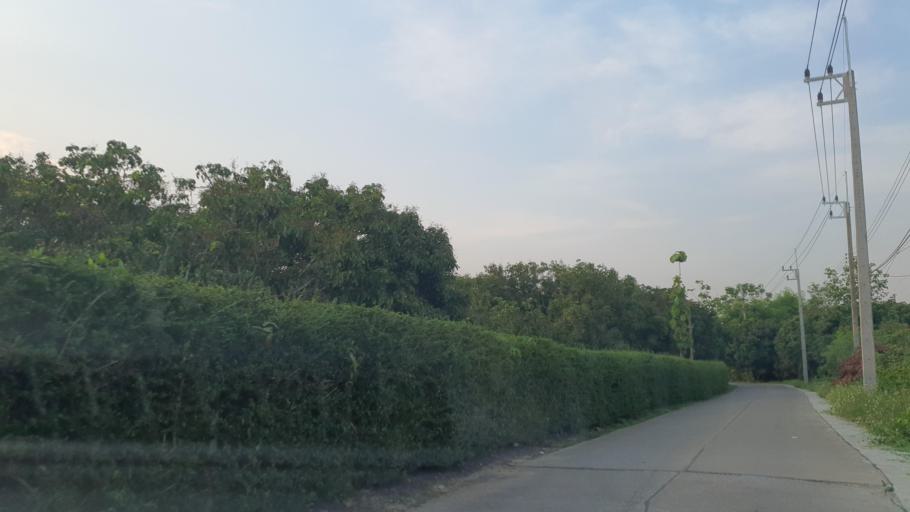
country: TH
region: Chiang Mai
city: Hang Dong
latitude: 18.6599
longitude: 98.9351
